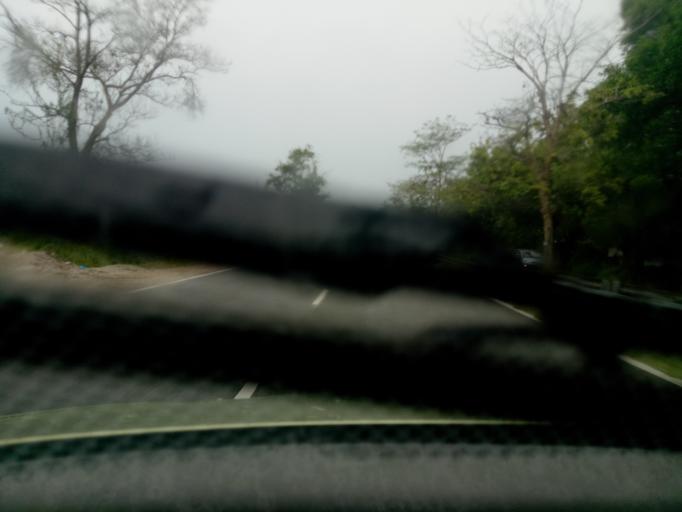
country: MY
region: Kedah
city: Sungai Petani
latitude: 5.6428
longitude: 100.5393
